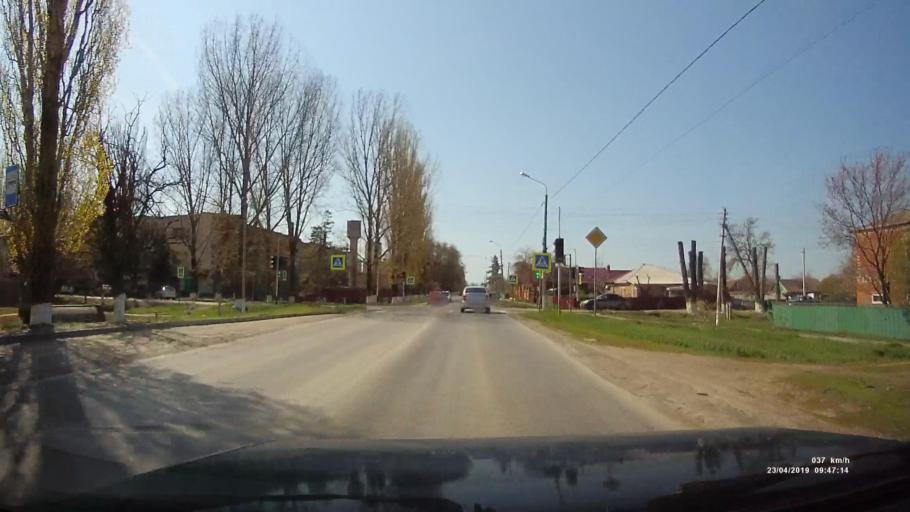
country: RU
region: Rostov
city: Orlovskiy
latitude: 46.8766
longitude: 42.0384
